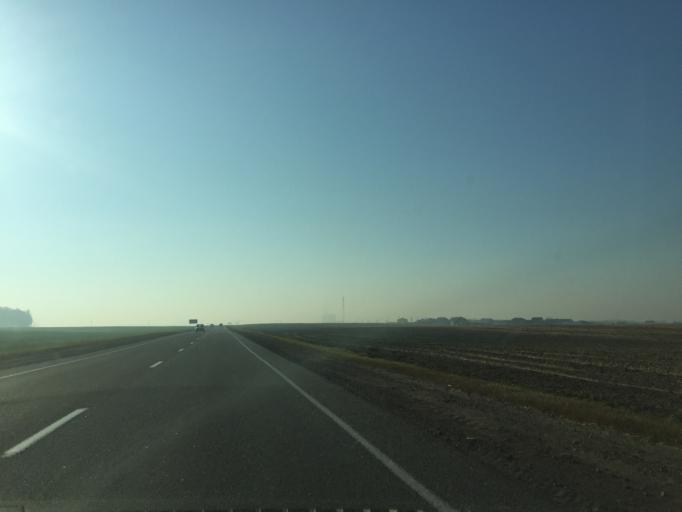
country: BY
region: Gomel
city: Kastsyukowka
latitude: 52.4848
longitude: 30.8198
